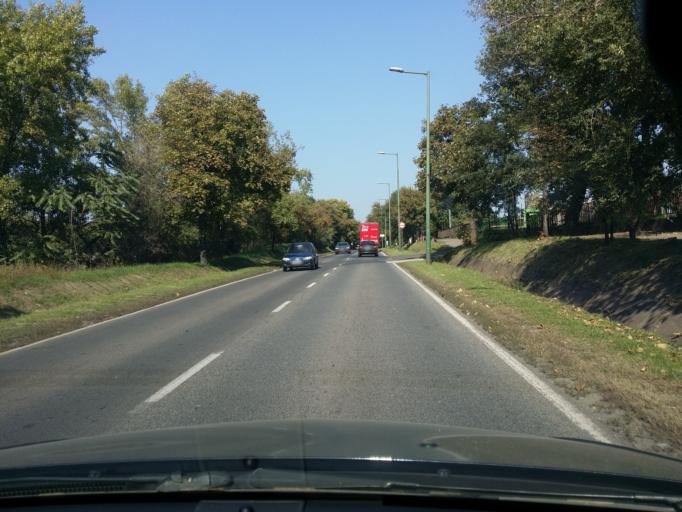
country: HU
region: Bacs-Kiskun
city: Dunavecse
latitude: 46.9357
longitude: 18.9520
